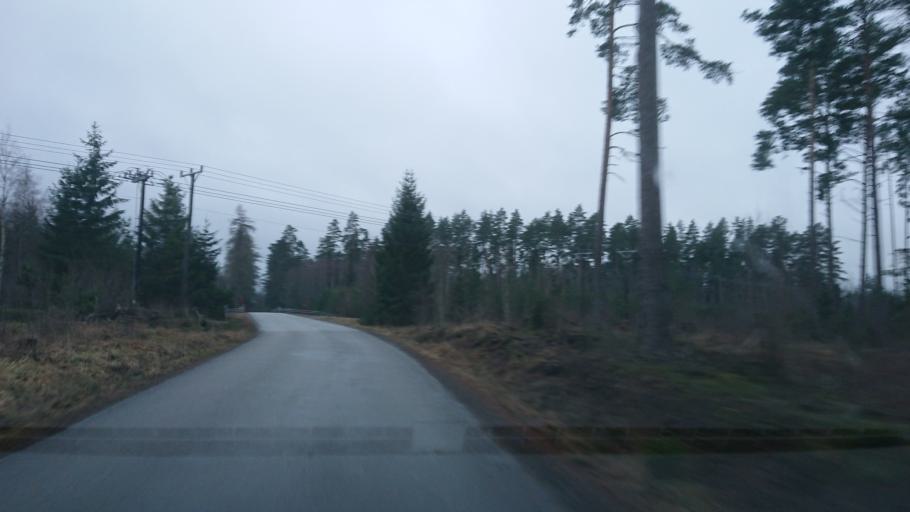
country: SE
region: Uppsala
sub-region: Osthammars Kommun
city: Bjorklinge
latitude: 60.0197
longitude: 17.5838
